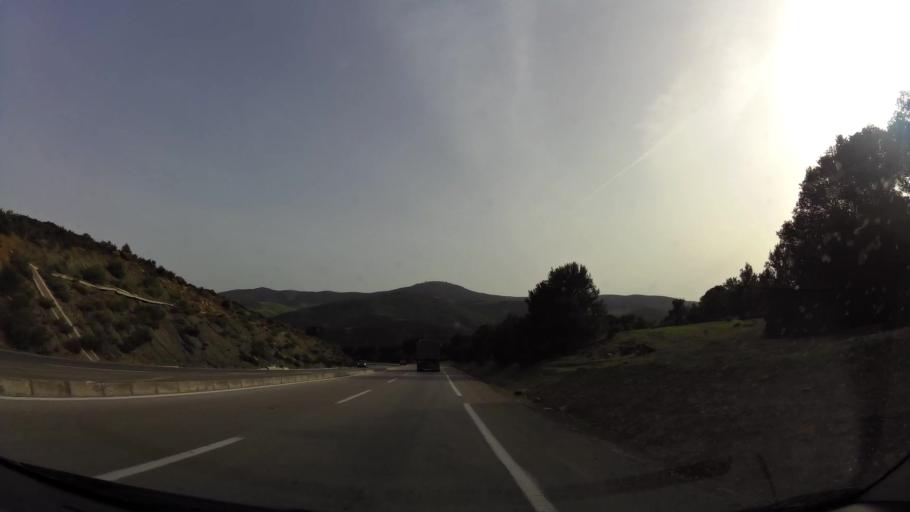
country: MA
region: Tanger-Tetouan
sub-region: Tetouan
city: Saddina
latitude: 35.5522
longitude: -5.5676
